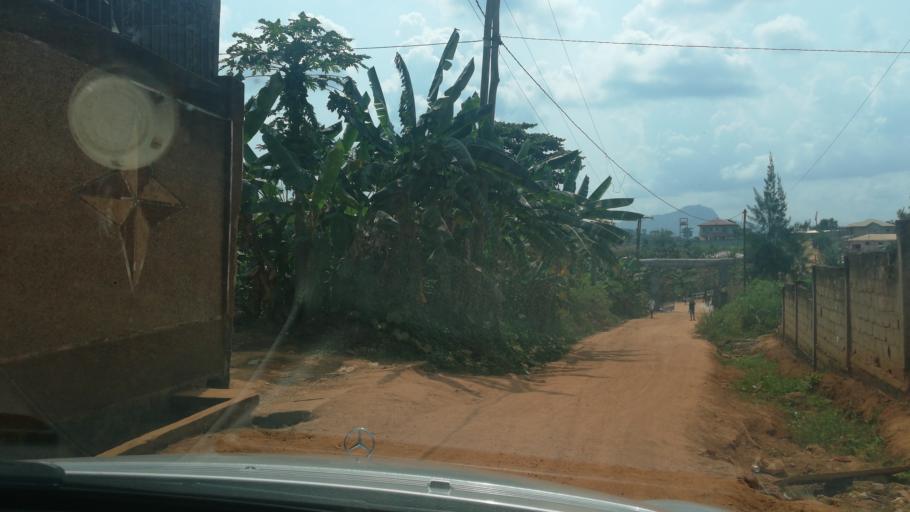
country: CM
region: Centre
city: Yaounde
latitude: 3.7855
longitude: 11.4890
